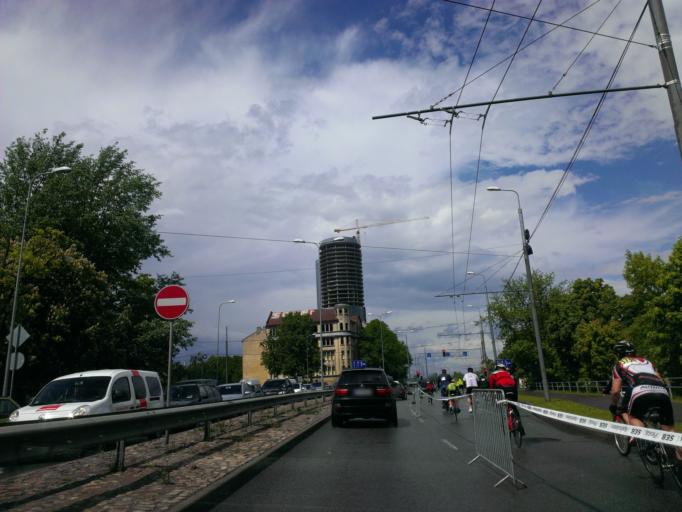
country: LV
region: Riga
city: Riga
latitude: 56.9438
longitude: 24.0852
